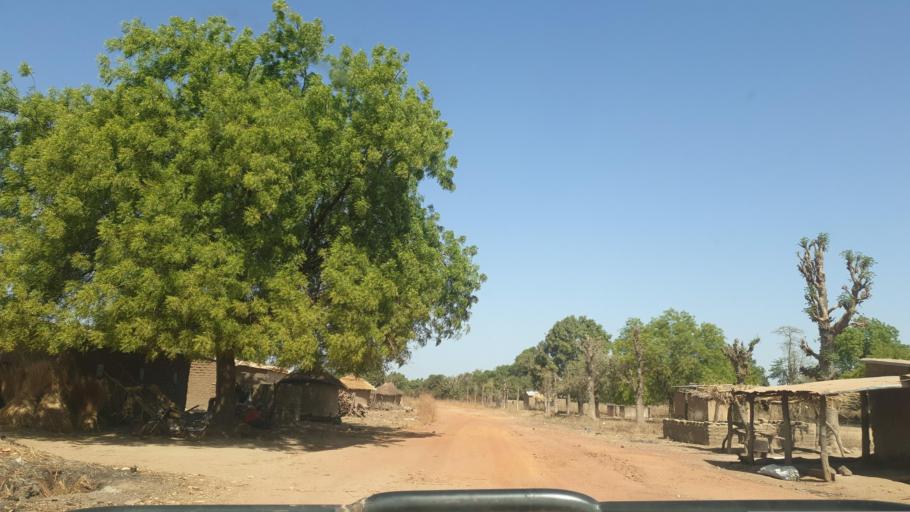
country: ML
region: Koulikoro
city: Dioila
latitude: 11.8955
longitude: -6.9803
